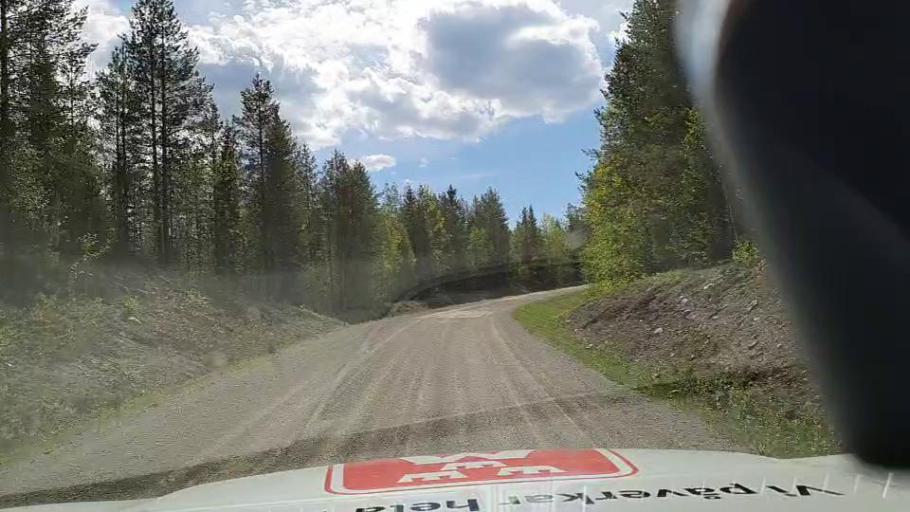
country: SE
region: Vaesterbotten
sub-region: Vilhelmina Kommun
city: Sjoberg
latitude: 64.5698
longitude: 15.8594
